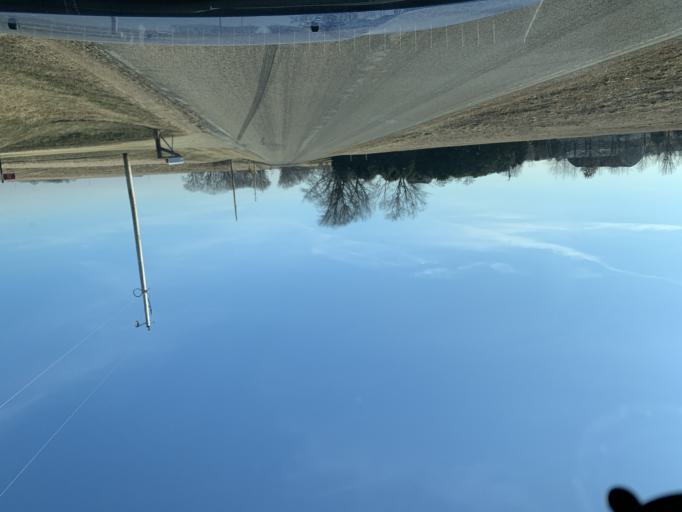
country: US
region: Wisconsin
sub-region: Iowa County
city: Barneveld
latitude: 42.8207
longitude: -89.9252
